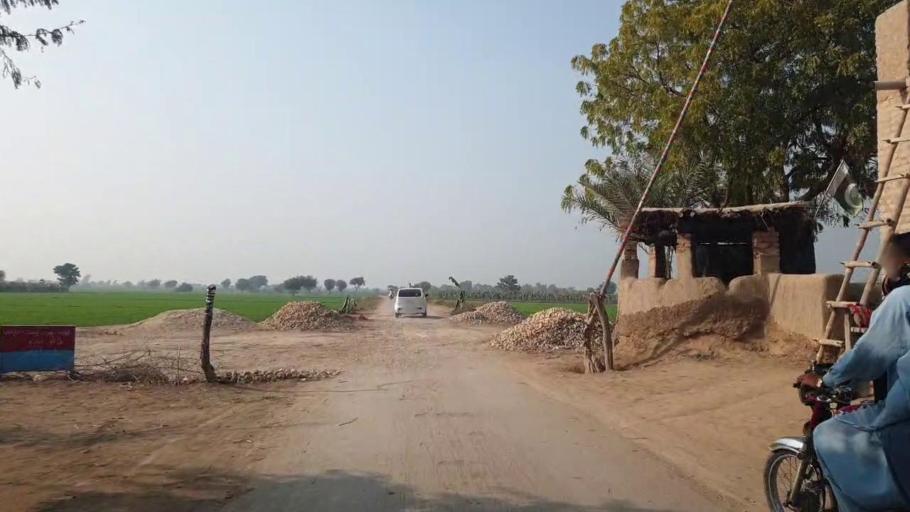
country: PK
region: Sindh
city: Shahdadpur
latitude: 25.9692
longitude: 68.5514
